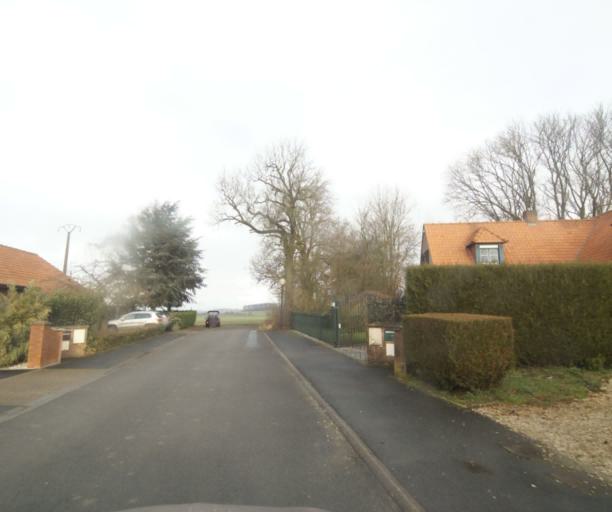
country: FR
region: Nord-Pas-de-Calais
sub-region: Departement du Nord
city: Famars
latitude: 50.2938
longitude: 3.5122
